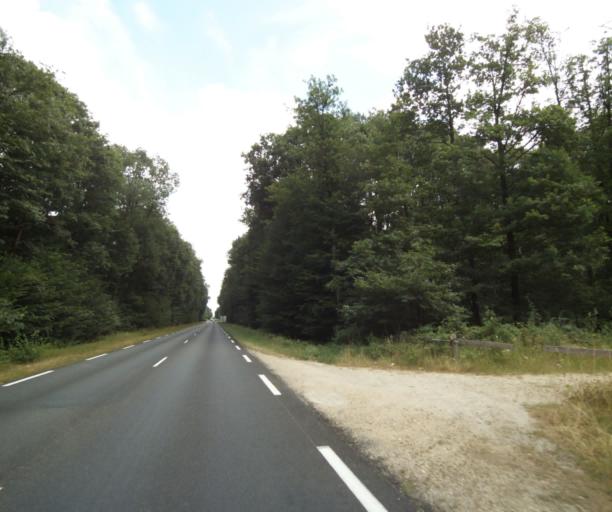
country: FR
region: Ile-de-France
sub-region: Departement de Seine-et-Marne
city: Thomery
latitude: 48.4208
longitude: 2.7862
